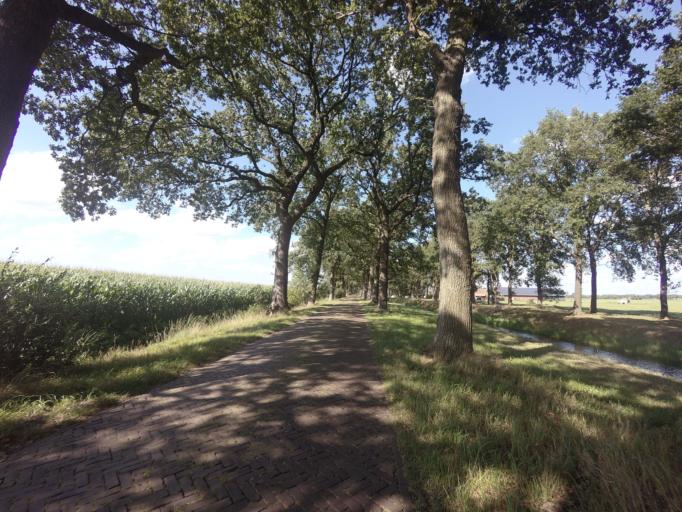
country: NL
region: Drenthe
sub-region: Gemeente Hoogeveen
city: Hoogeveen
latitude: 52.6598
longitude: 6.5148
